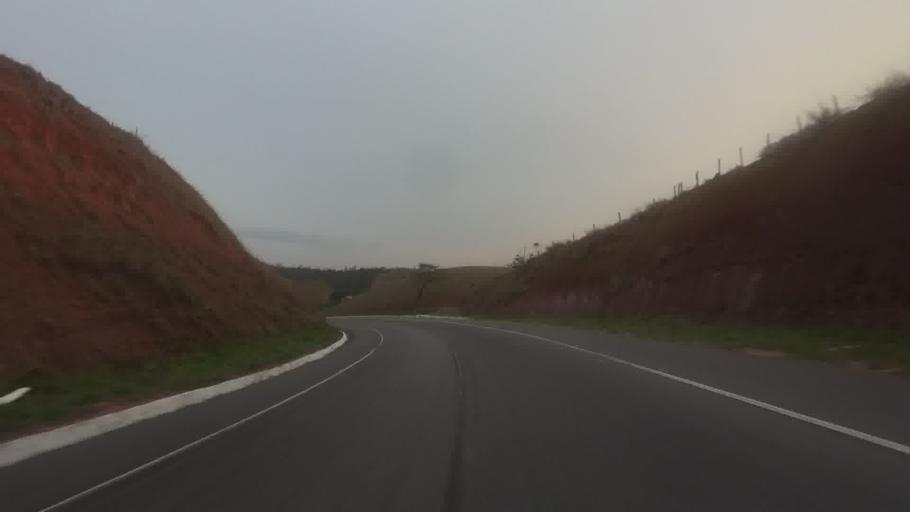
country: BR
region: Minas Gerais
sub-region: Recreio
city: Recreio
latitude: -21.7258
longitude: -42.4446
